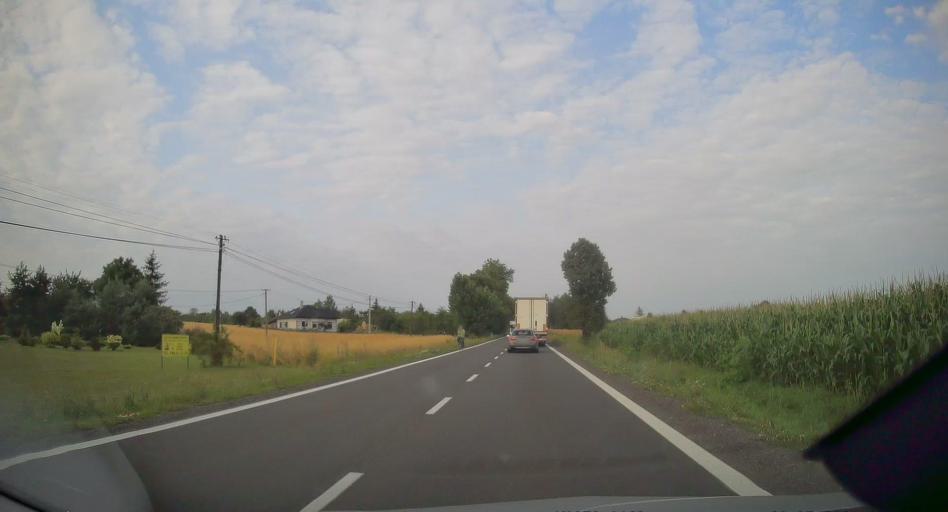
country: PL
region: Silesian Voivodeship
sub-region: Powiat czestochowski
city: Borowno
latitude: 50.9041
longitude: 19.2928
